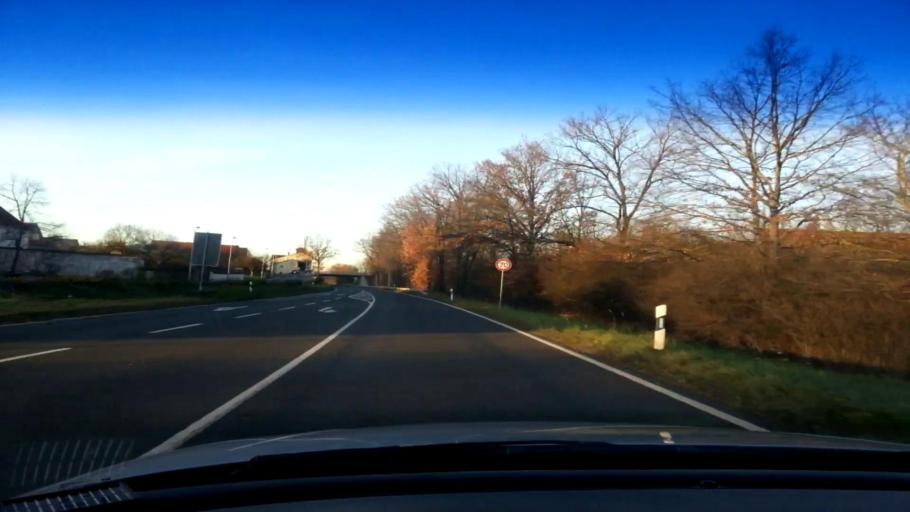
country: DE
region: Bavaria
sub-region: Upper Franconia
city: Rattelsdorf
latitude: 50.0143
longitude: 10.8911
